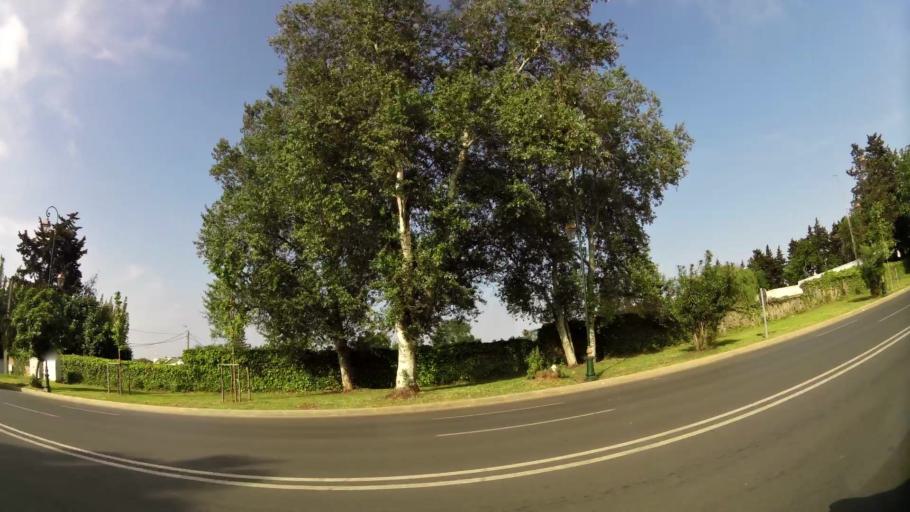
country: MA
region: Rabat-Sale-Zemmour-Zaer
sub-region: Rabat
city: Rabat
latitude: 33.9465
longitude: -6.8102
